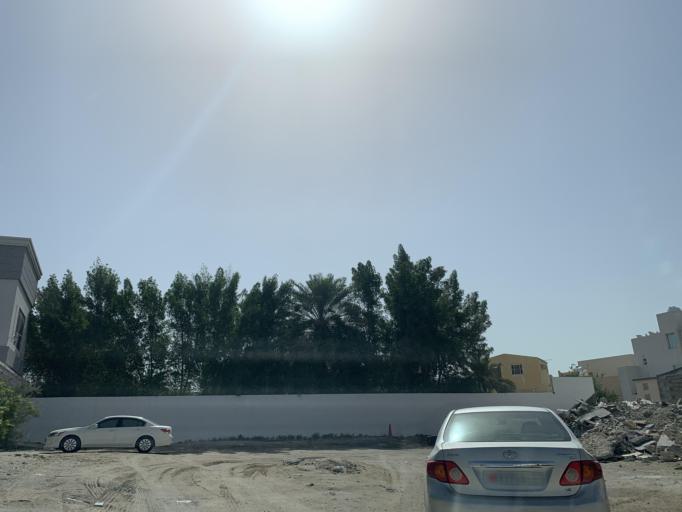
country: BH
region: Northern
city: Sitrah
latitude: 26.1468
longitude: 50.6054
